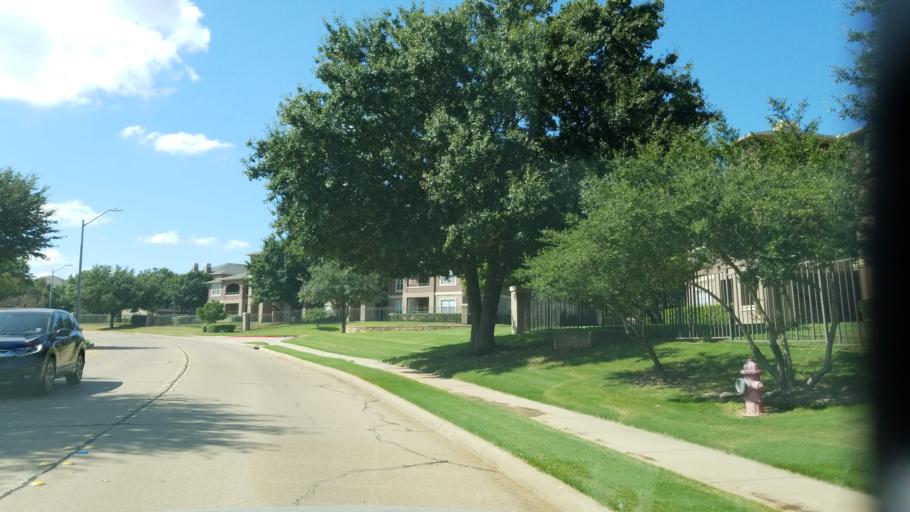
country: US
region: Texas
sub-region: Tarrant County
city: Euless
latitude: 32.8558
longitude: -97.0710
